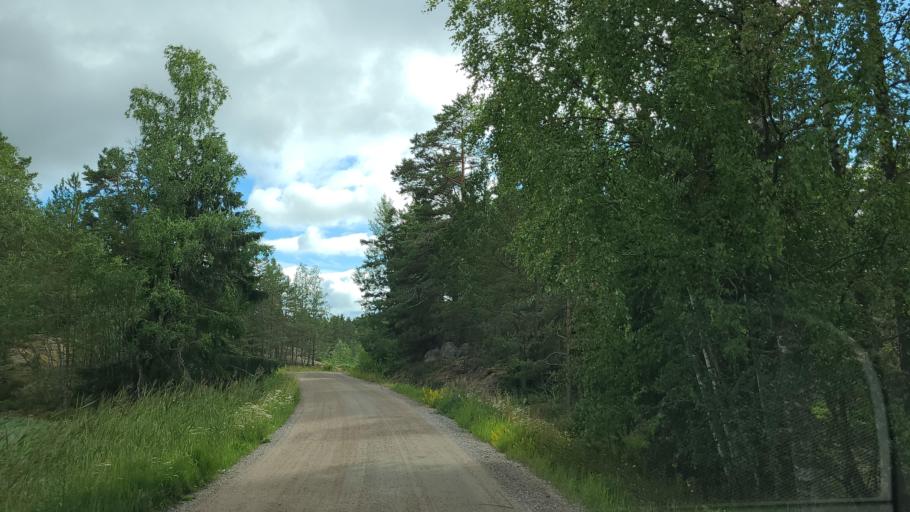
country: FI
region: Varsinais-Suomi
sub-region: Aboland-Turunmaa
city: Nagu
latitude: 60.2022
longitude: 21.7912
